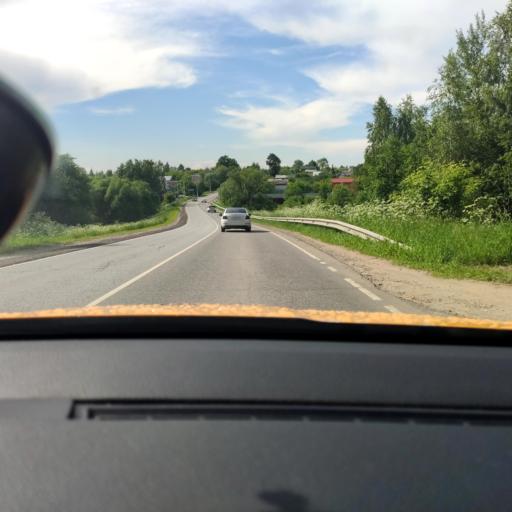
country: RU
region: Moskovskaya
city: Zhilevo
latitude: 54.9614
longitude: 37.9895
